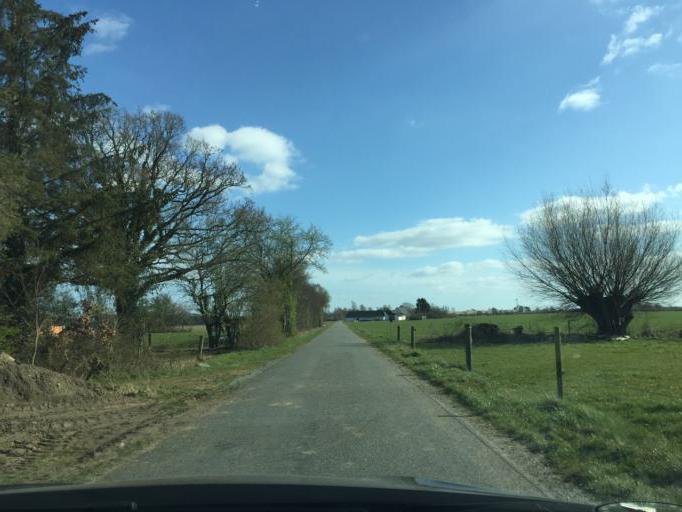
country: DK
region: South Denmark
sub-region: Kerteminde Kommune
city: Langeskov
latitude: 55.3028
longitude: 10.5646
